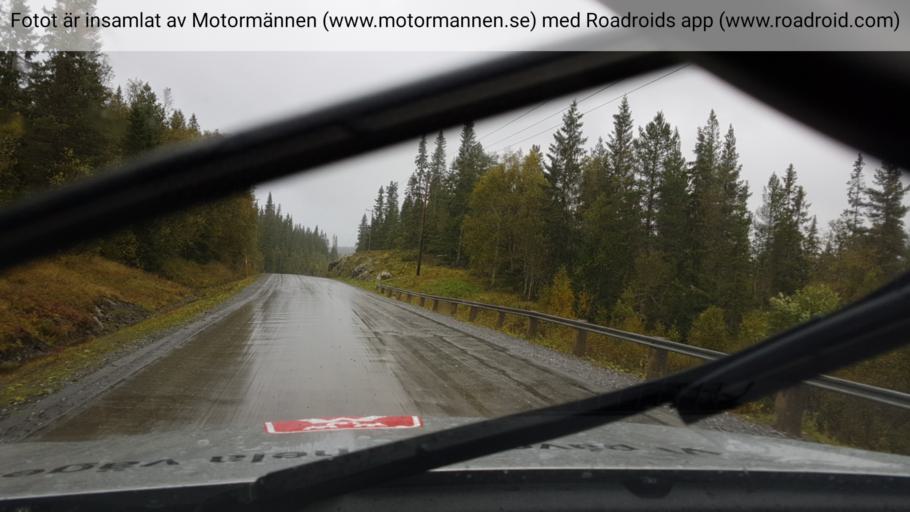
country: SE
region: Jaemtland
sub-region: Are Kommun
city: Are
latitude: 63.6790
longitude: 12.8134
